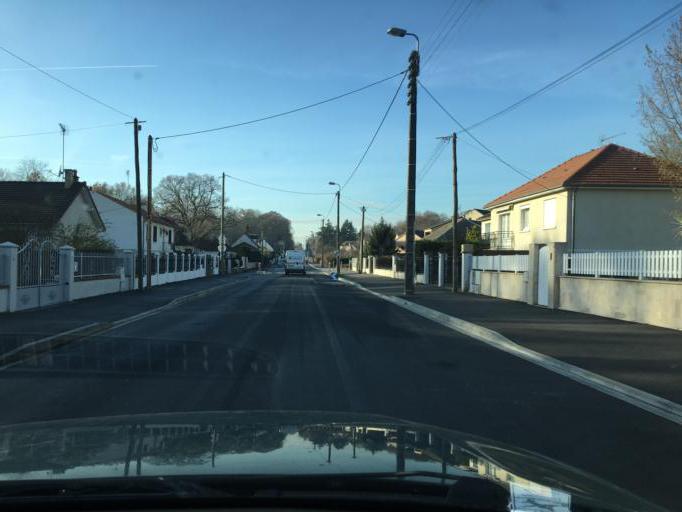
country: FR
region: Centre
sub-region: Departement du Loiret
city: Saran
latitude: 47.9505
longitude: 1.8721
